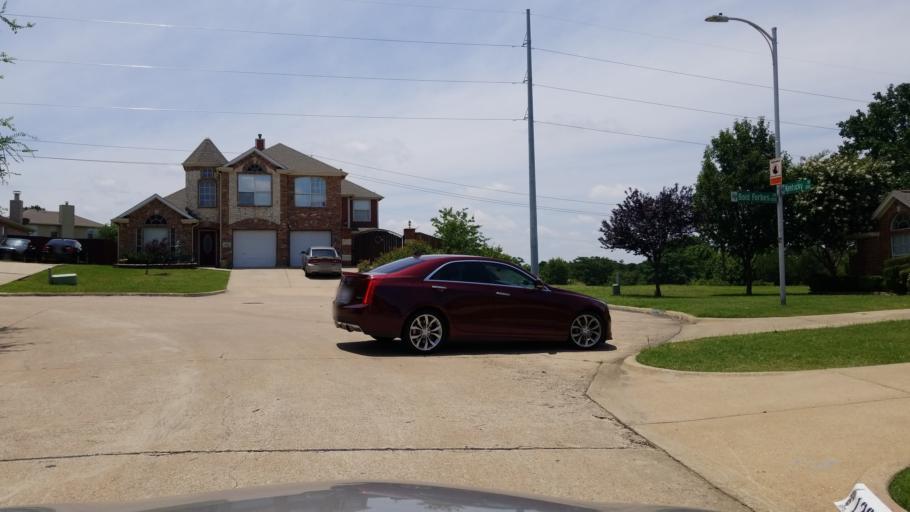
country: US
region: Texas
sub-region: Dallas County
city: Grand Prairie
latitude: 32.6819
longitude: -96.9902
